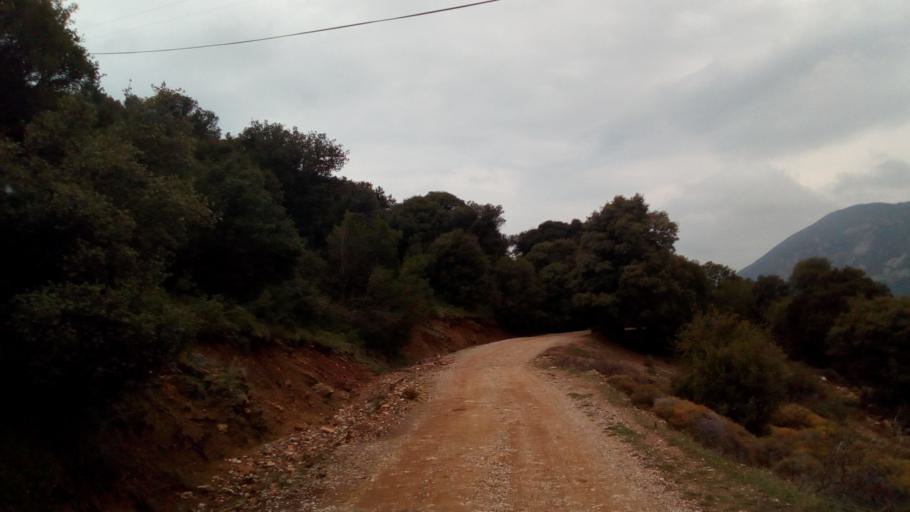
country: GR
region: West Greece
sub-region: Nomos Achaias
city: Selianitika
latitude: 38.4010
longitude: 22.0838
